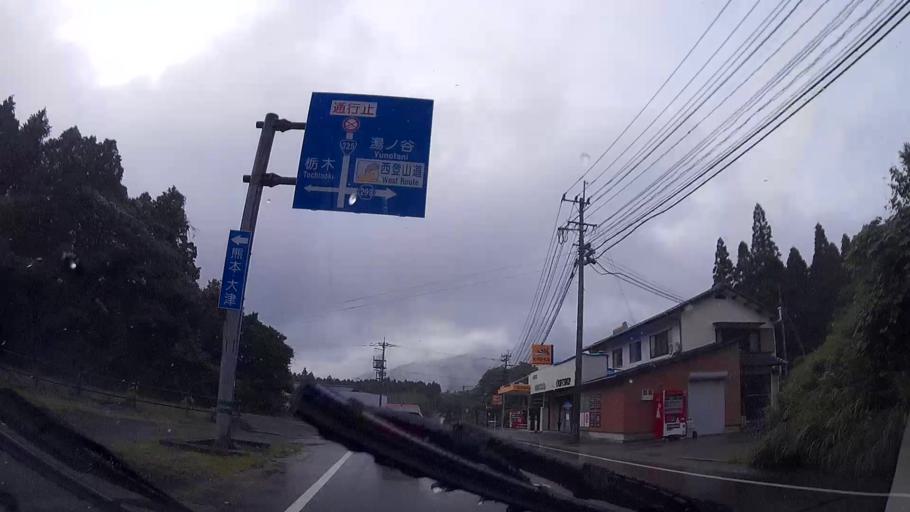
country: JP
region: Kumamoto
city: Aso
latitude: 32.8703
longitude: 130.9958
